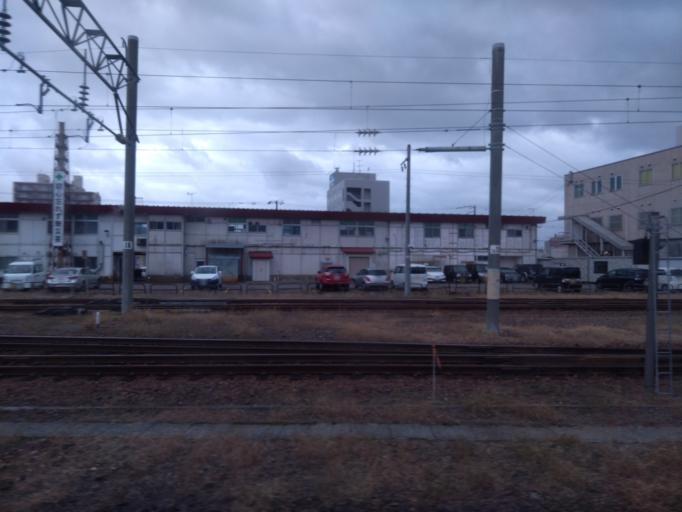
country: JP
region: Hokkaido
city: Hakodate
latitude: 41.7764
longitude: 140.7279
